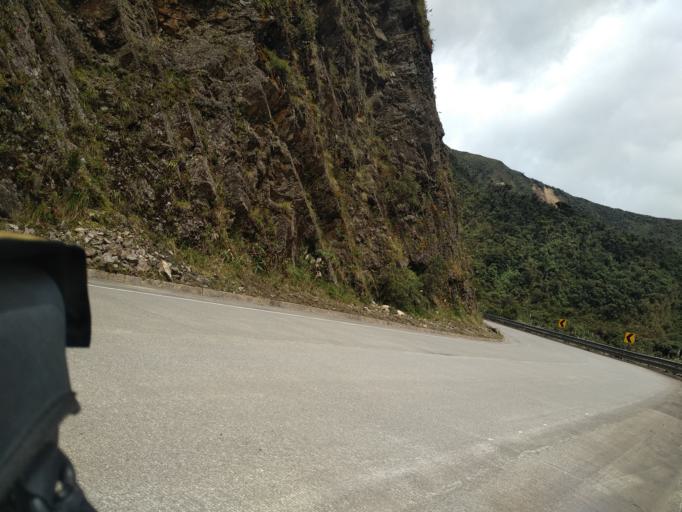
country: EC
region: Zamora-Chinchipe
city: Zamora
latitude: -4.4327
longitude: -79.1499
